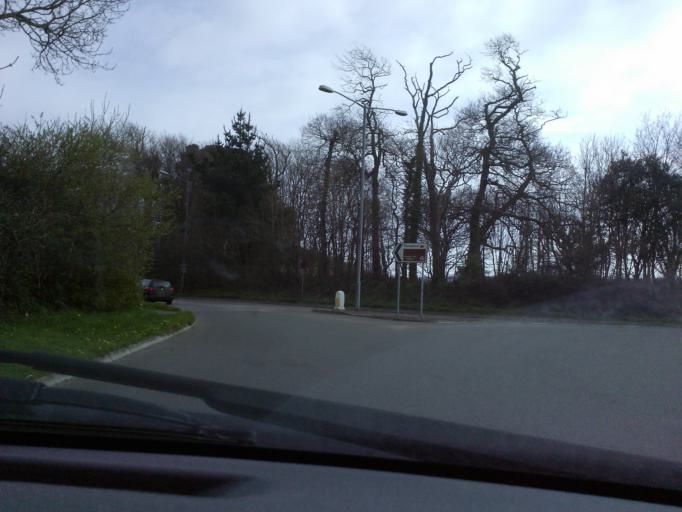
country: GB
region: England
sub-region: Cornwall
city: Penzance
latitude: 50.1142
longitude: -5.5571
